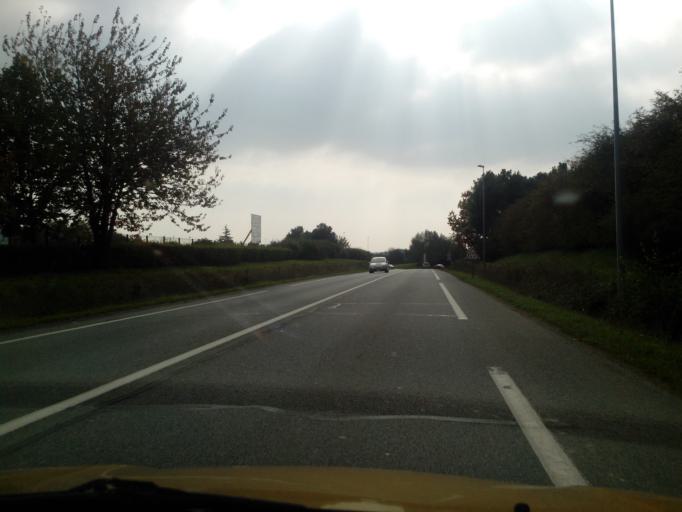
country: FR
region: Brittany
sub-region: Departement du Morbihan
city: Ploermel
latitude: 47.9353
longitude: -2.3815
